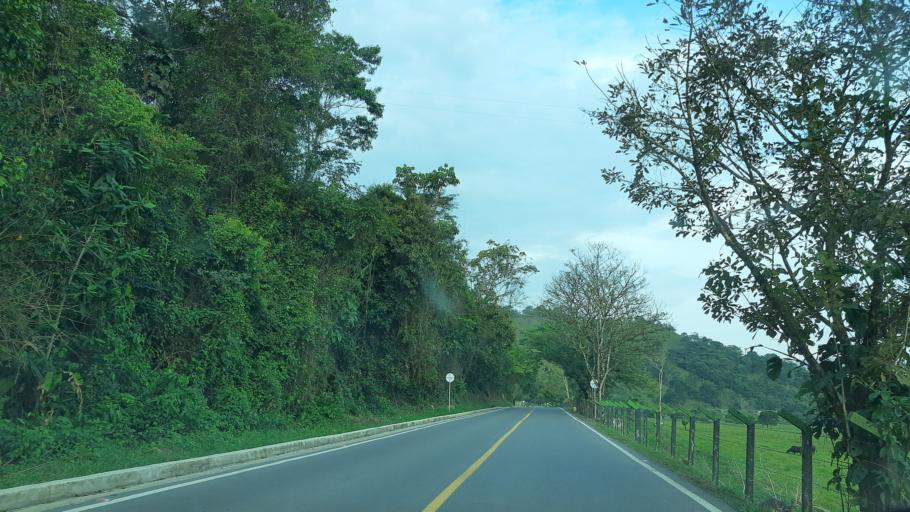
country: CO
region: Boyaca
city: San Luis de Gaceno
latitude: 4.8227
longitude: -73.1971
